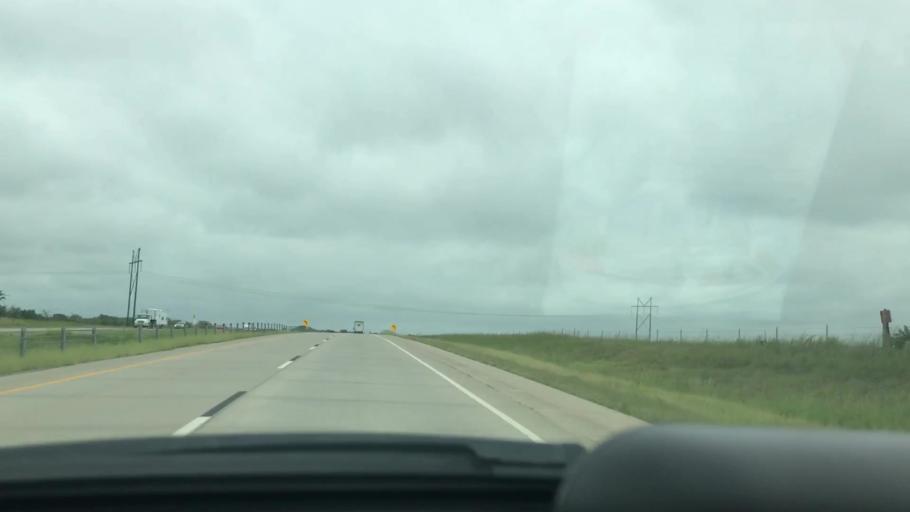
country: US
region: Oklahoma
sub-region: Pittsburg County
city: McAlester
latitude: 34.6876
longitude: -95.9178
